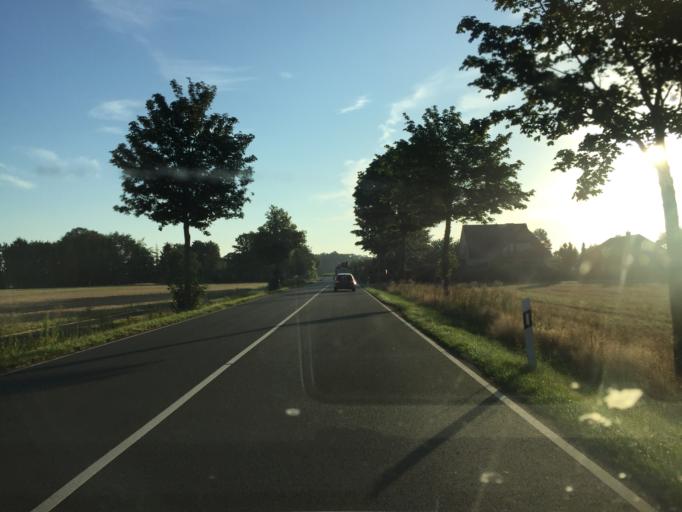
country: DE
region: Lower Saxony
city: Heemsen
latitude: 52.7165
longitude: 9.2798
